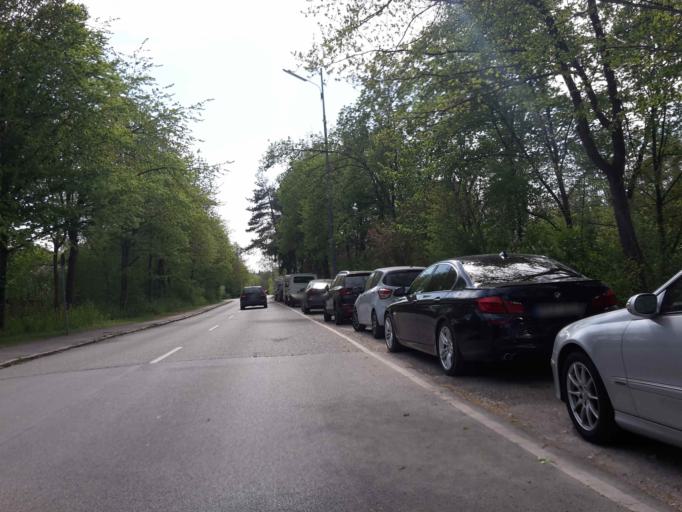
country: DE
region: Bavaria
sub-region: Upper Bavaria
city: Pasing
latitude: 48.1726
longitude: 11.4986
